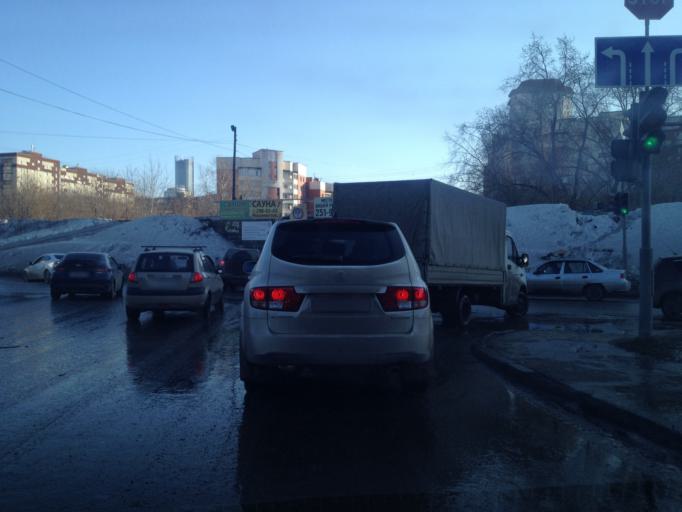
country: RU
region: Sverdlovsk
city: Yekaterinburg
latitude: 56.8559
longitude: 60.5819
